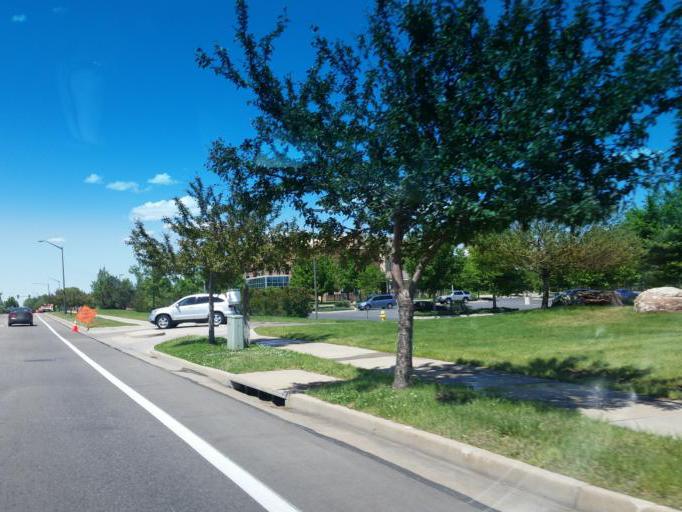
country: US
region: Colorado
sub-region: Larimer County
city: Fort Collins
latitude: 40.5317
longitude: -105.0961
